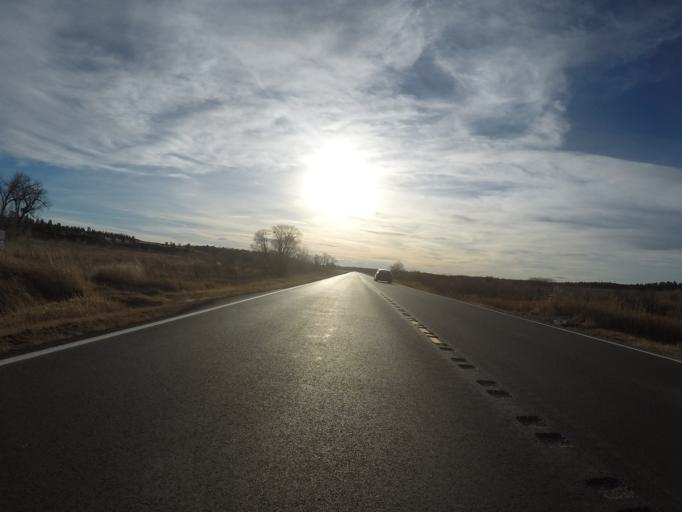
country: US
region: Montana
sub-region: Musselshell County
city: Roundup
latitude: 46.3563
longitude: -108.6690
